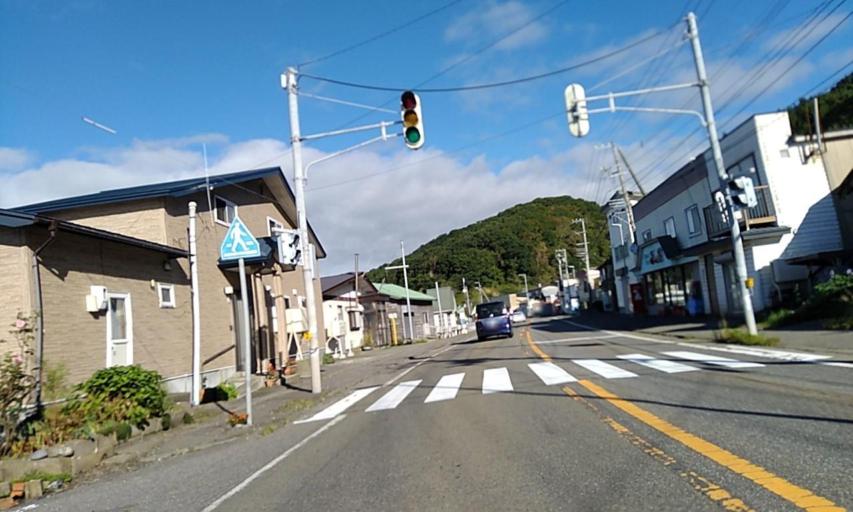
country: JP
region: Hokkaido
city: Shizunai-furukawacho
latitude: 42.2709
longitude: 142.4849
